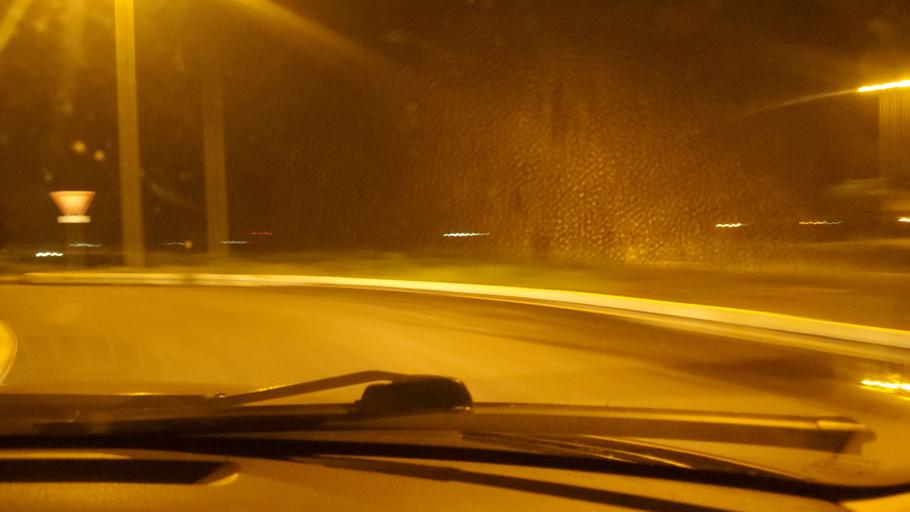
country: SN
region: Thies
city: Pout
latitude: 14.6649
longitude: -17.0654
